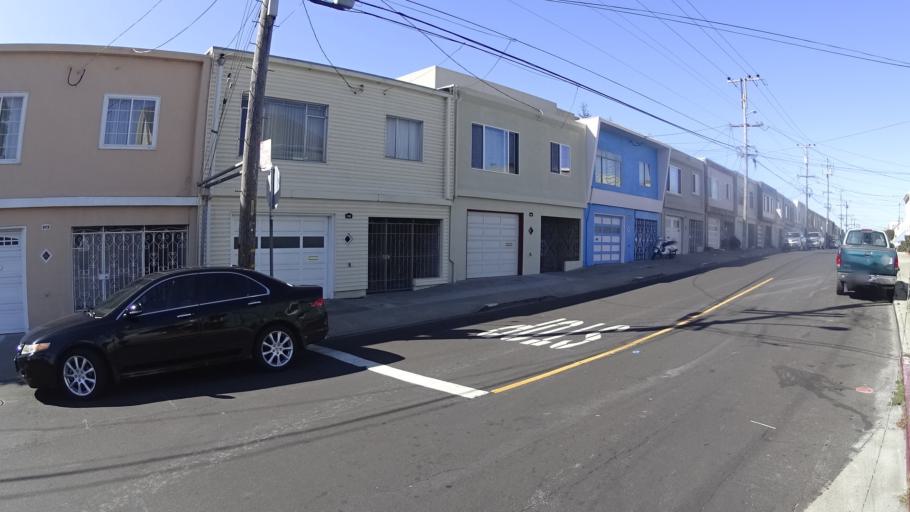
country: US
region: California
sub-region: San Mateo County
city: Daly City
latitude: 37.7020
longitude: -122.4694
